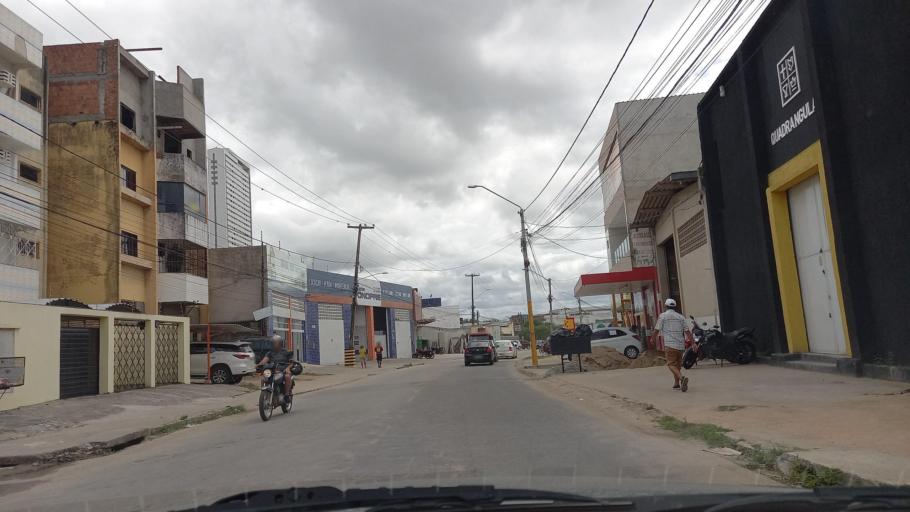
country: BR
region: Pernambuco
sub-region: Caruaru
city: Caruaru
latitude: -8.2686
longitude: -35.9615
